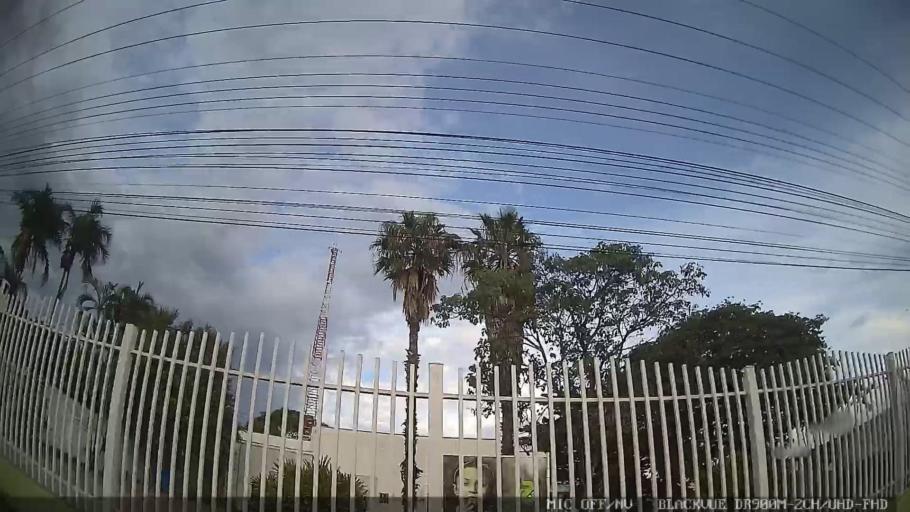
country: BR
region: Sao Paulo
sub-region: Jaguariuna
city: Jaguariuna
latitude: -22.6322
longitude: -47.0485
